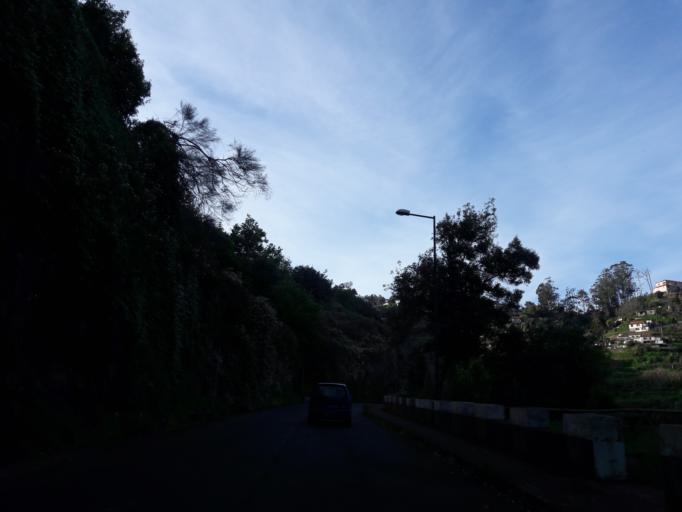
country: PT
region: Madeira
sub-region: Santa Cruz
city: Camacha
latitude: 32.6651
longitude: -16.8496
